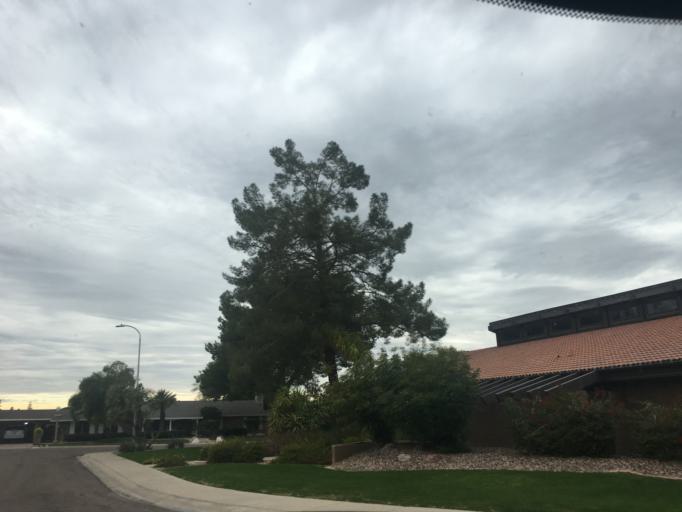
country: US
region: Arizona
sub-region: Maricopa County
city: Guadalupe
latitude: 33.3648
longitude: -111.9248
